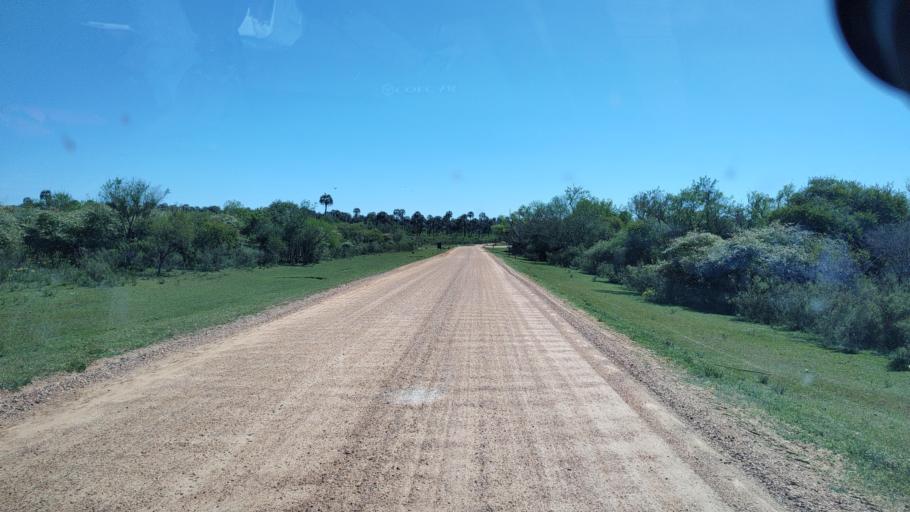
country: AR
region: Entre Rios
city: Ubajay
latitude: -31.8738
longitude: -58.2273
